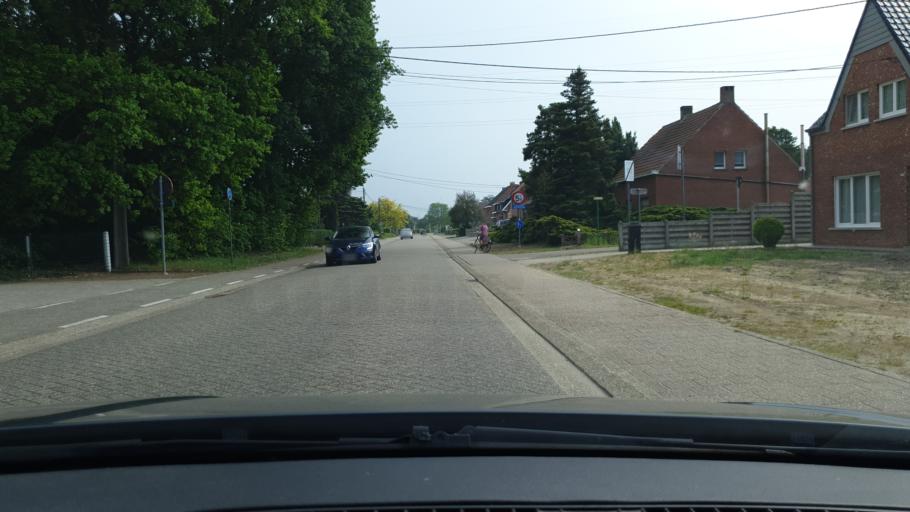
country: BE
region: Flanders
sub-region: Provincie Antwerpen
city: Olen
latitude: 51.1756
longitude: 4.8819
